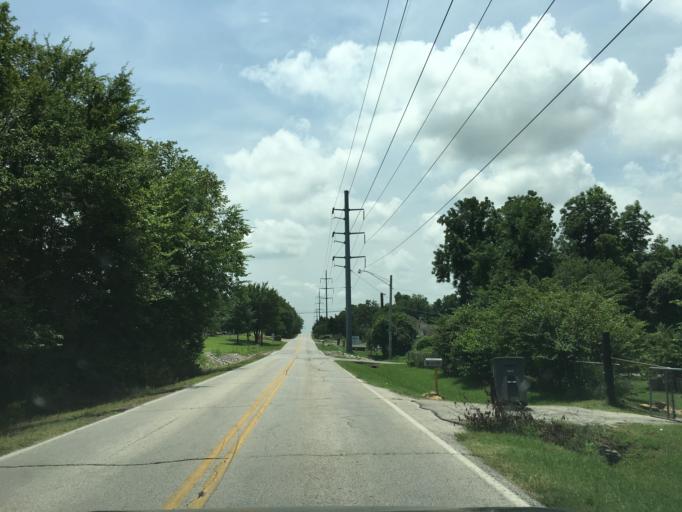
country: US
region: Oklahoma
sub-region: Tulsa County
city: Jenks
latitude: 36.0662
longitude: -95.9938
